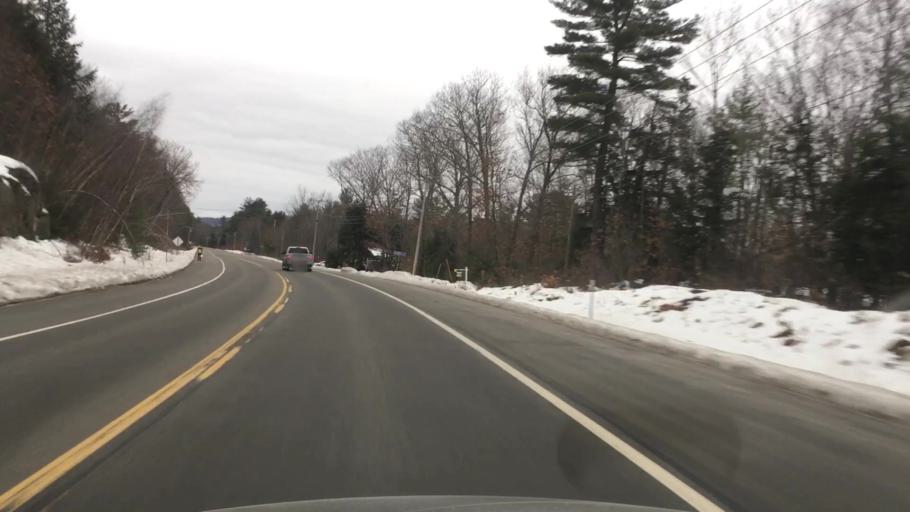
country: US
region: New Hampshire
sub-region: Merrimack County
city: Sutton
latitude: 43.2827
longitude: -71.9761
